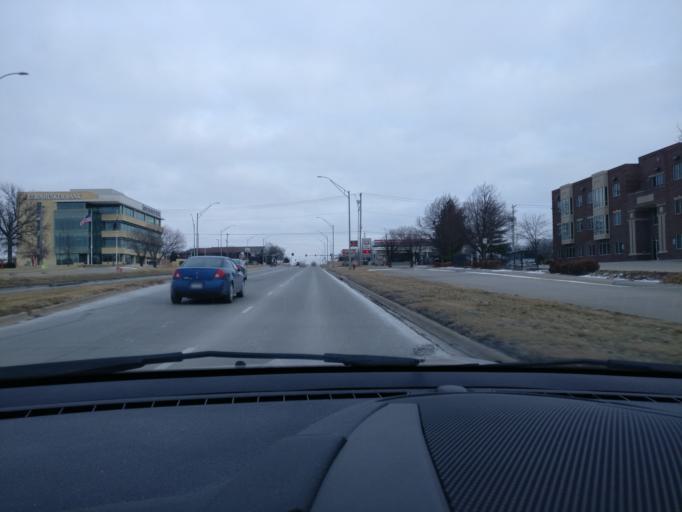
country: US
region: Nebraska
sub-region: Lancaster County
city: Lincoln
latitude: 40.8134
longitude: -96.6096
